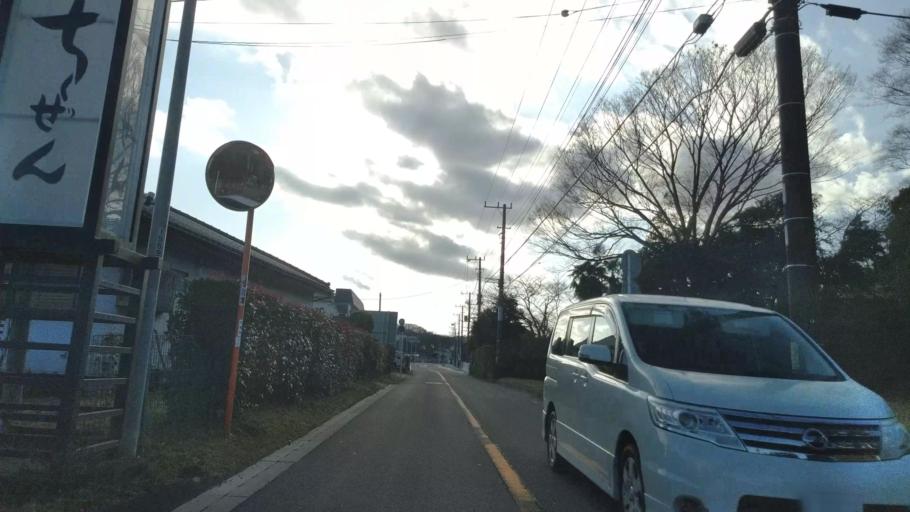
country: JP
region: Kanagawa
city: Hadano
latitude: 35.3515
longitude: 139.2623
